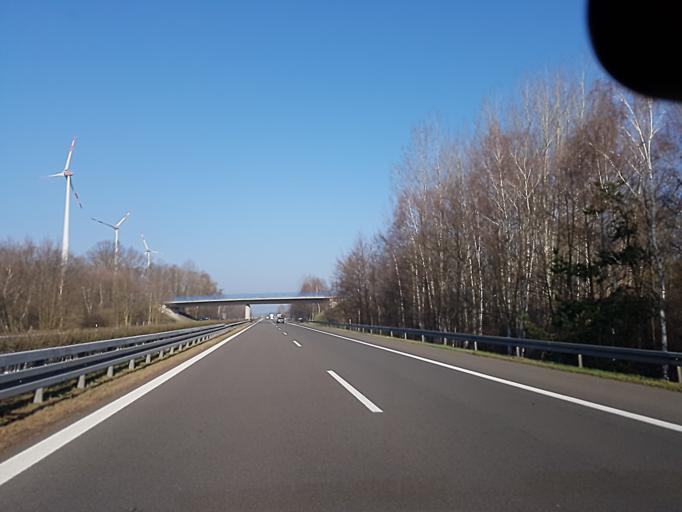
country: DE
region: Brandenburg
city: Forst
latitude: 51.7016
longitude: 14.6509
